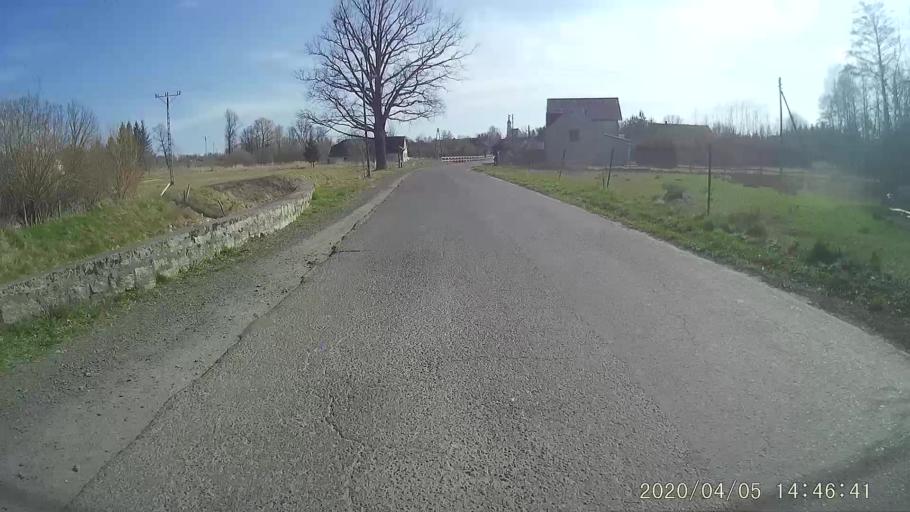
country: PL
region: Lower Silesian Voivodeship
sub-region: Powiat zgorzelecki
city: Sulikow
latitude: 51.0593
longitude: 15.1095
